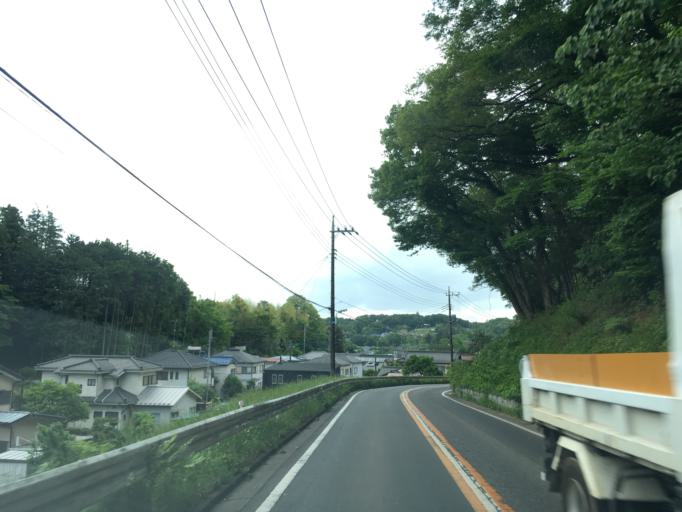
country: JP
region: Saitama
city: Tokorozawa
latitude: 35.7815
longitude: 139.4174
